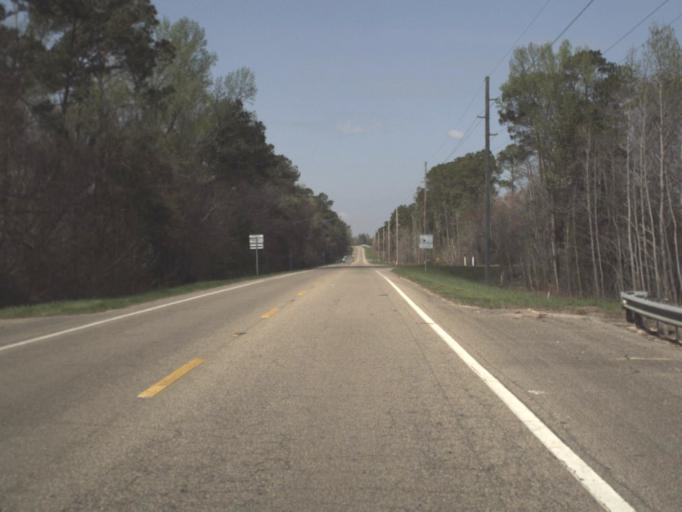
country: US
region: Florida
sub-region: Liberty County
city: Bristol
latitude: 30.4275
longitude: -84.9305
